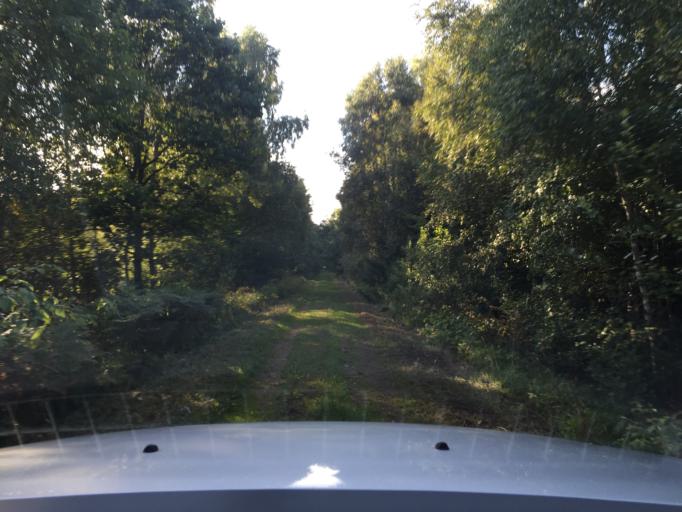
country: SE
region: Skane
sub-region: Hassleholms Kommun
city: Sosdala
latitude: 56.0169
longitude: 13.7188
